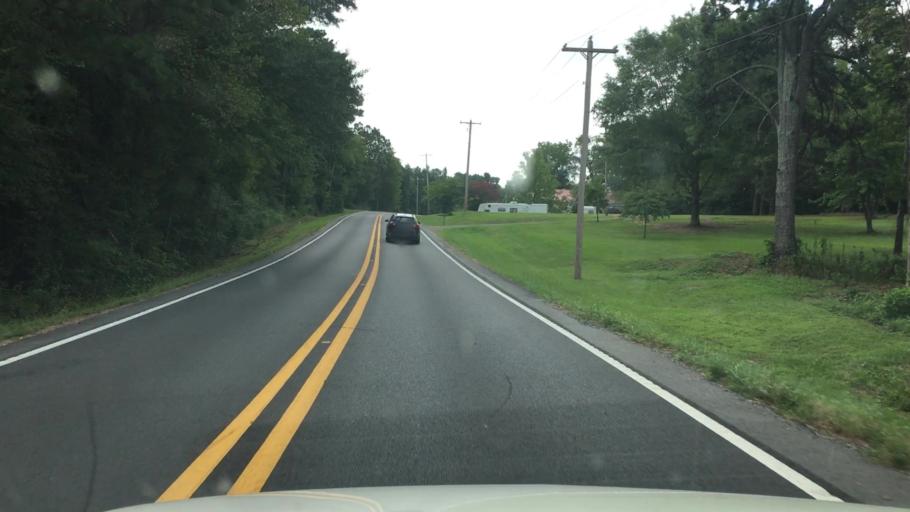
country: US
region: Arkansas
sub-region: Garland County
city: Lake Hamilton
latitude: 34.3026
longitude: -93.1659
